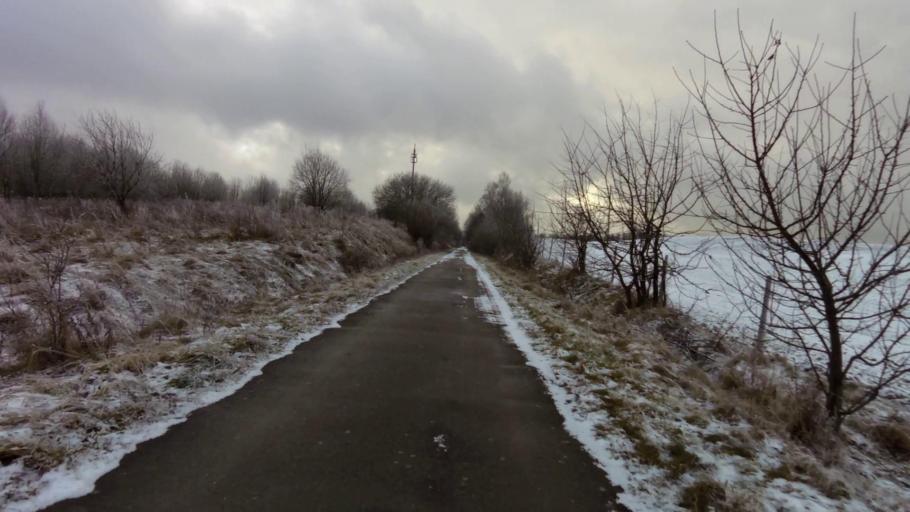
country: PL
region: West Pomeranian Voivodeship
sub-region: Powiat swidwinski
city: Polczyn-Zdroj
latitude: 53.7157
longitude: 16.0393
